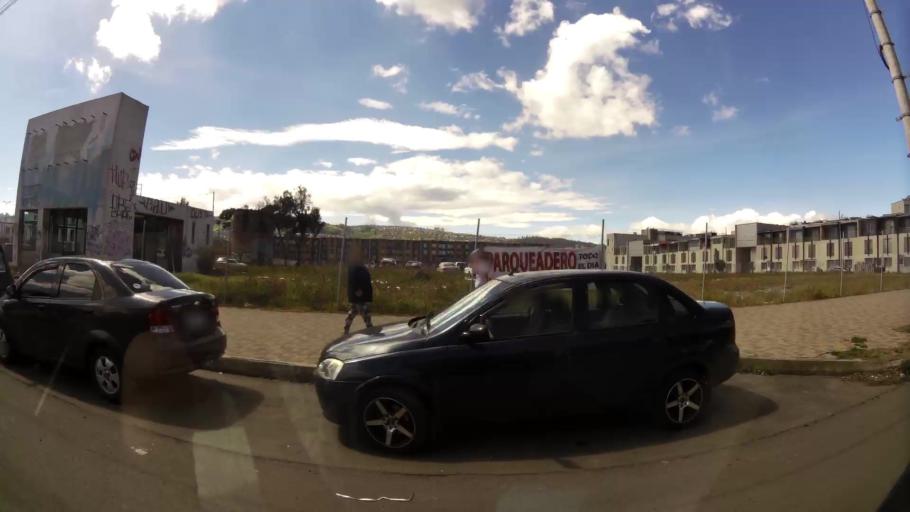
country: EC
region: Pichincha
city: Quito
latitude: -0.2962
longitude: -78.5493
